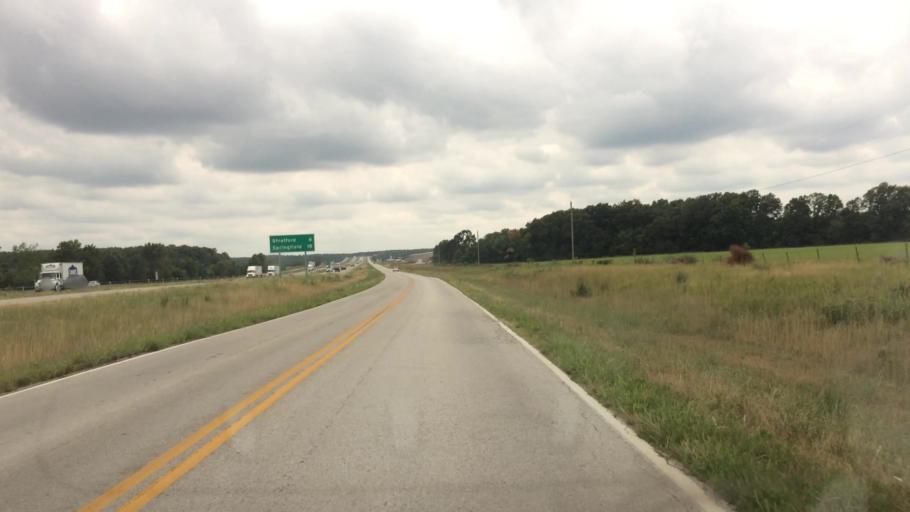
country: US
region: Missouri
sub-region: Greene County
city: Strafford
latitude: 37.2998
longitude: -93.0129
